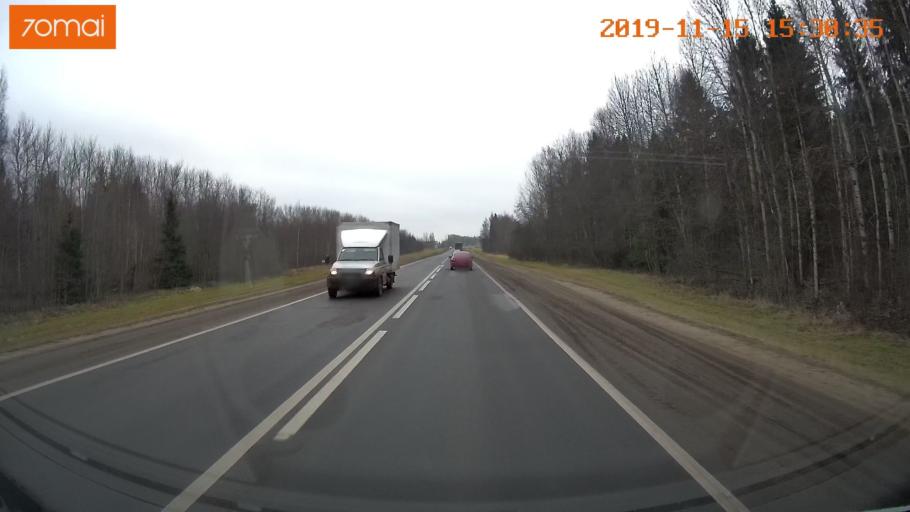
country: RU
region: Jaroslavl
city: Danilov
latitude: 58.1088
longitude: 40.1123
